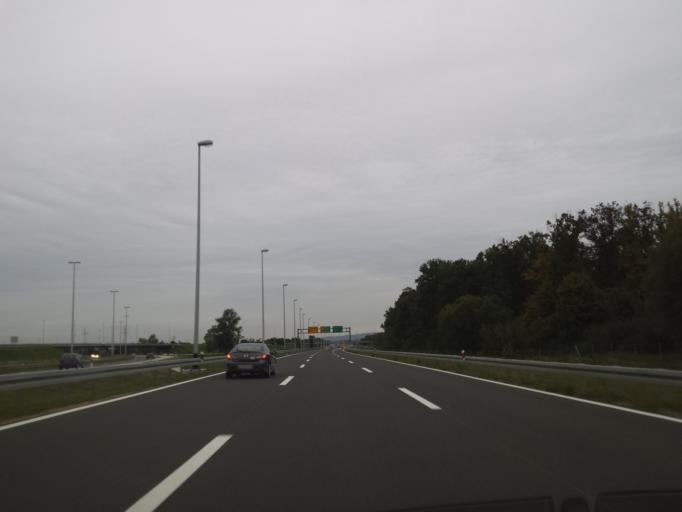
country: HR
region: Grad Zagreb
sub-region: Sesvete
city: Sesvete
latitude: 45.7981
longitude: 16.1423
